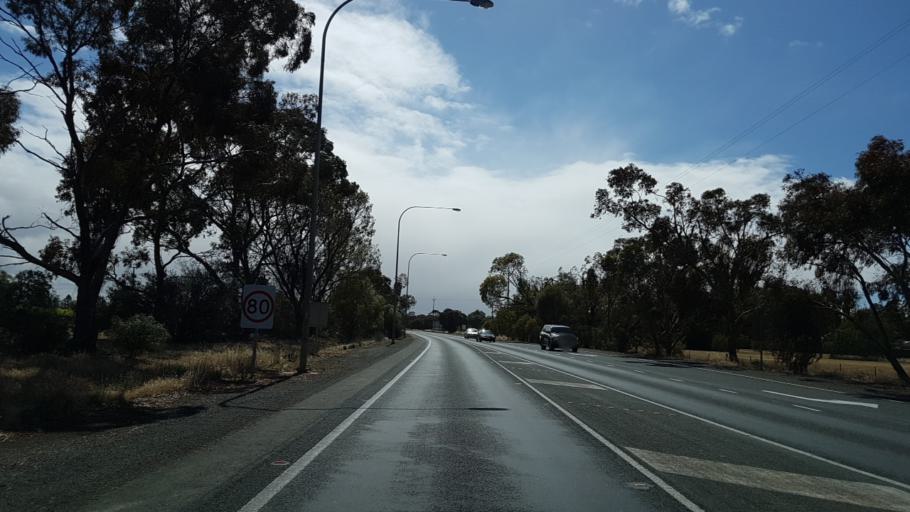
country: AU
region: South Australia
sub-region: Barossa
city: Nuriootpa
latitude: -34.4561
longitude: 139.0038
